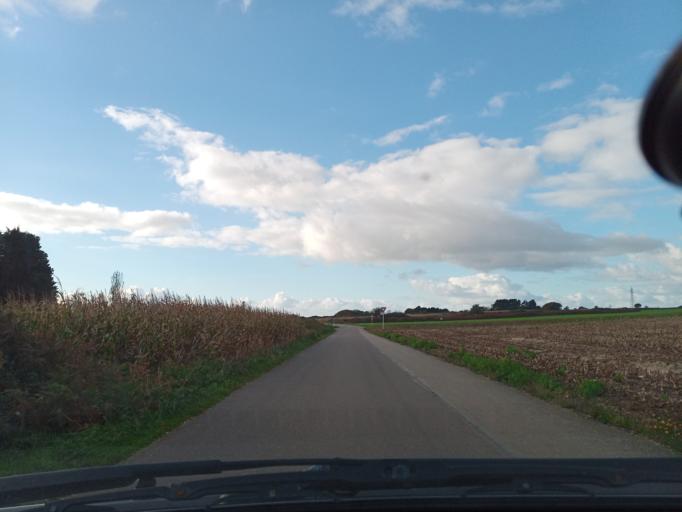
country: FR
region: Brittany
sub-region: Departement du Finistere
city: Plouhinec
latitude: 48.0182
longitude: -4.4978
